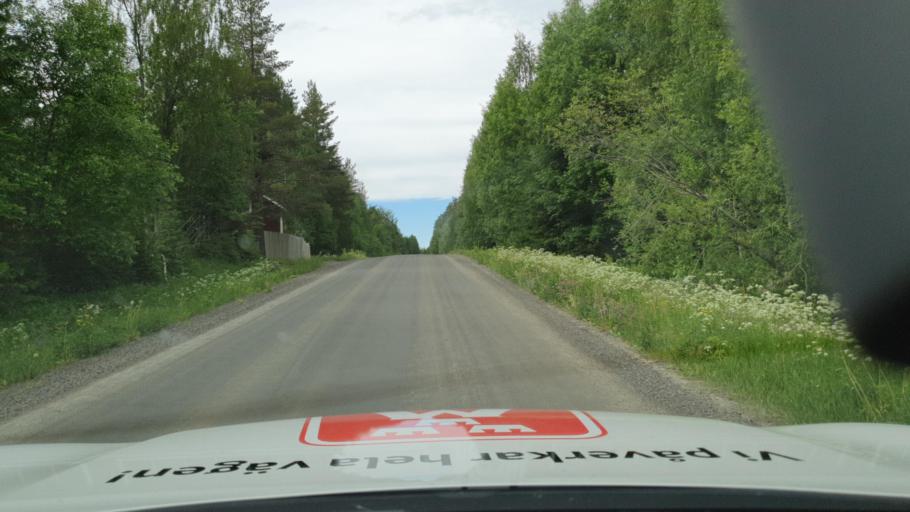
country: SE
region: Vaesterbotten
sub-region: Skelleftea Kommun
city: Burtraesk
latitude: 64.3685
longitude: 20.3929
